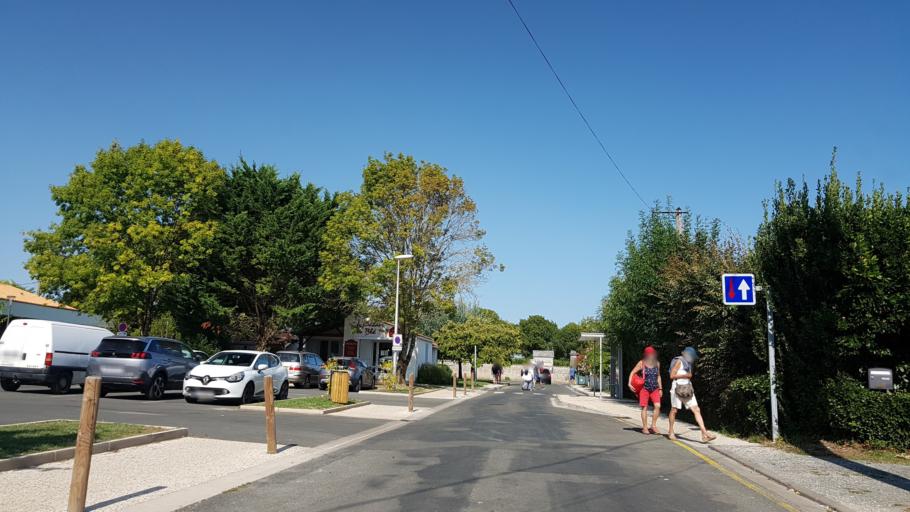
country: FR
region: Poitou-Charentes
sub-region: Departement de la Charente-Maritime
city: Breuillet
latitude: 45.7075
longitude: -1.0286
